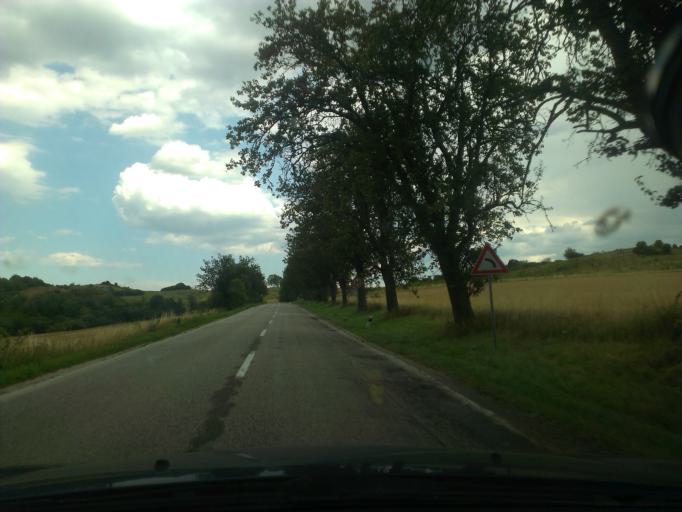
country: SK
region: Trenciansky
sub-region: Okres Myjava
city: Myjava
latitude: 48.7543
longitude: 17.5836
